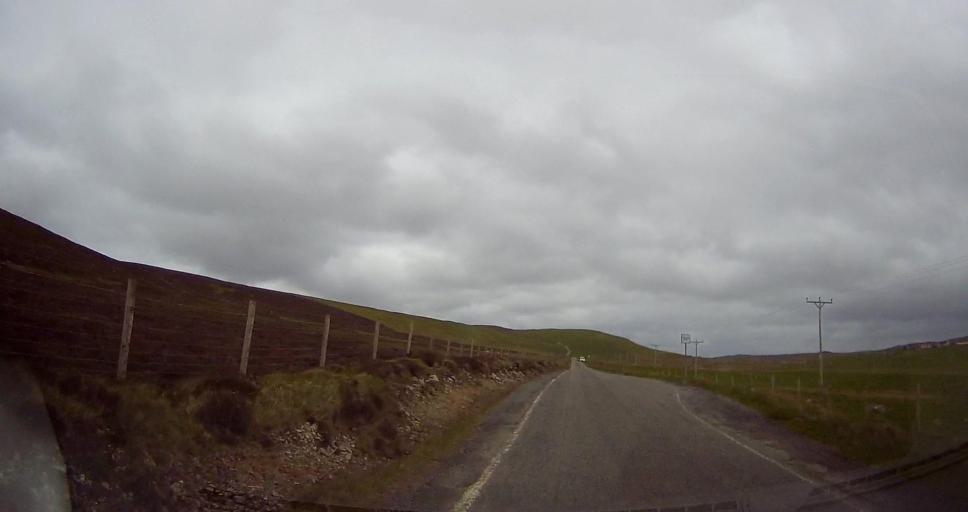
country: GB
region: Scotland
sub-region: Shetland Islands
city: Sandwick
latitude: 60.2455
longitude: -1.5110
